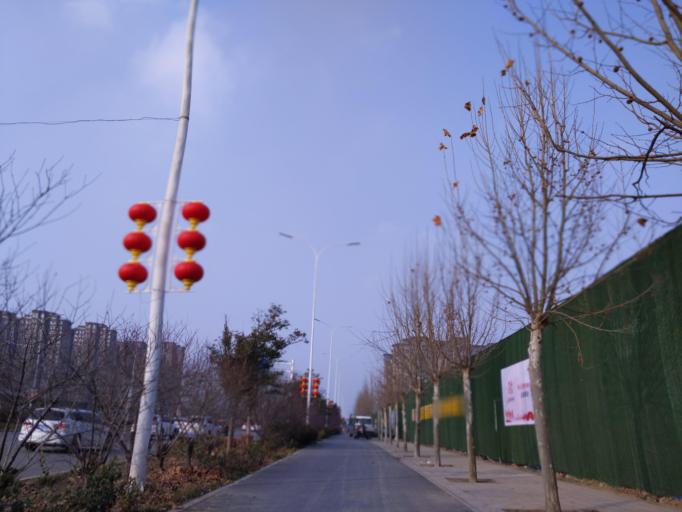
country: CN
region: Henan Sheng
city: Puyang
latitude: 35.8117
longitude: 115.0225
